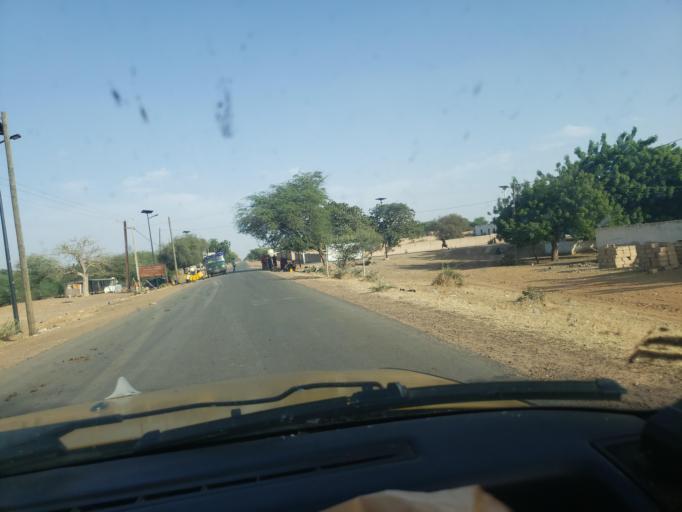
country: SN
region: Louga
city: Louga
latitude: 15.5120
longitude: -15.9908
